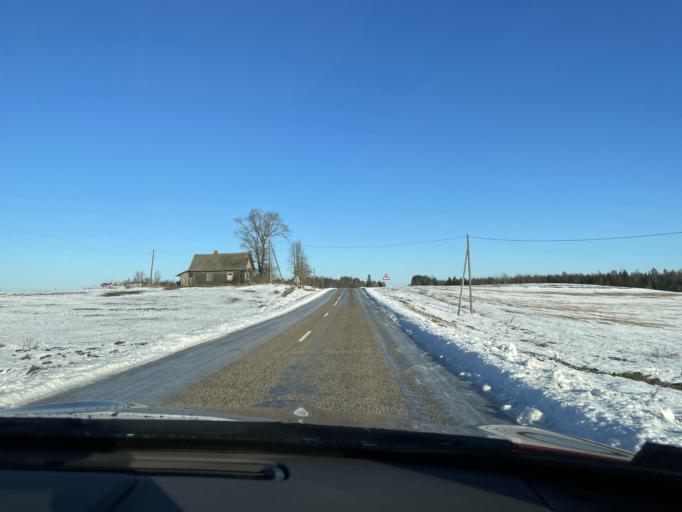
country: LV
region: Ludzas Rajons
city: Ludza
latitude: 56.4440
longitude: 27.5422
